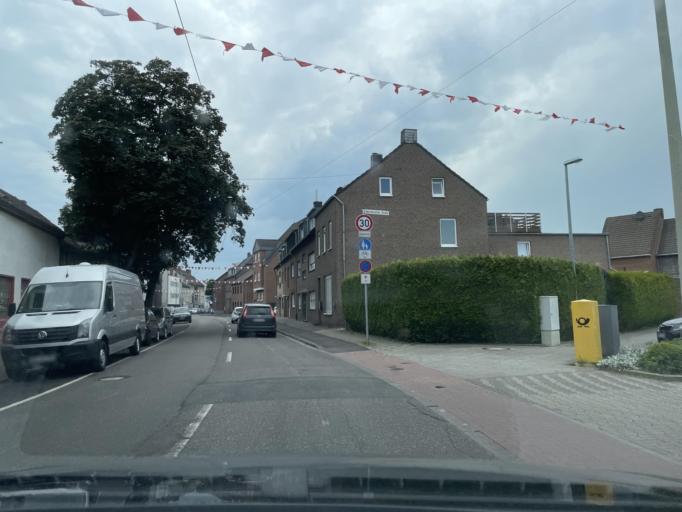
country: DE
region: North Rhine-Westphalia
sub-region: Regierungsbezirk Dusseldorf
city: Korschenbroich
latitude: 51.2223
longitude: 6.4772
